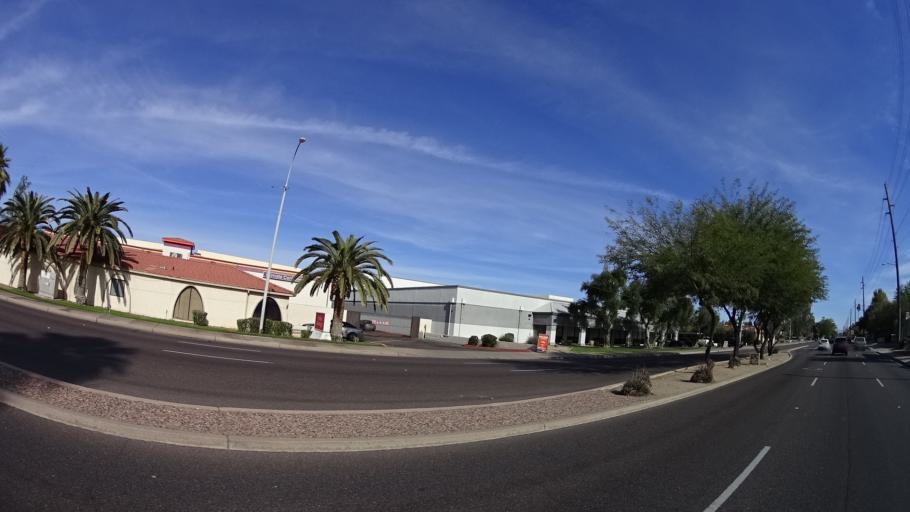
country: US
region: Arizona
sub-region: Maricopa County
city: Tempe
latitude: 33.4074
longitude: -111.9038
